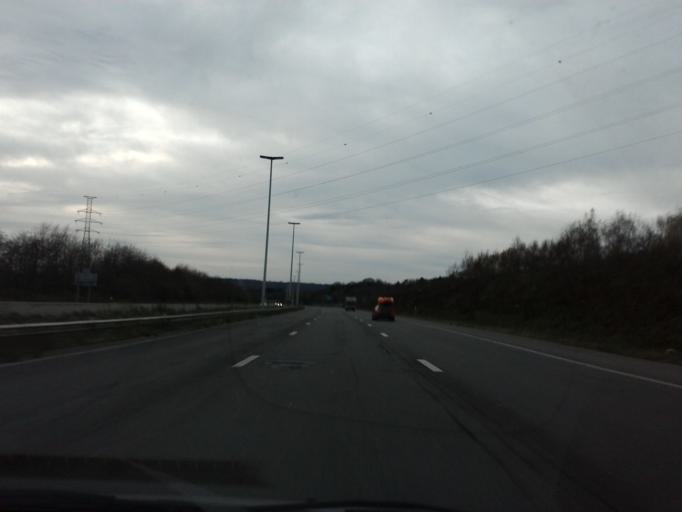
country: BE
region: Wallonia
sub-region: Province de Liege
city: Chaudfontaine
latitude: 50.5596
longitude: 5.6158
